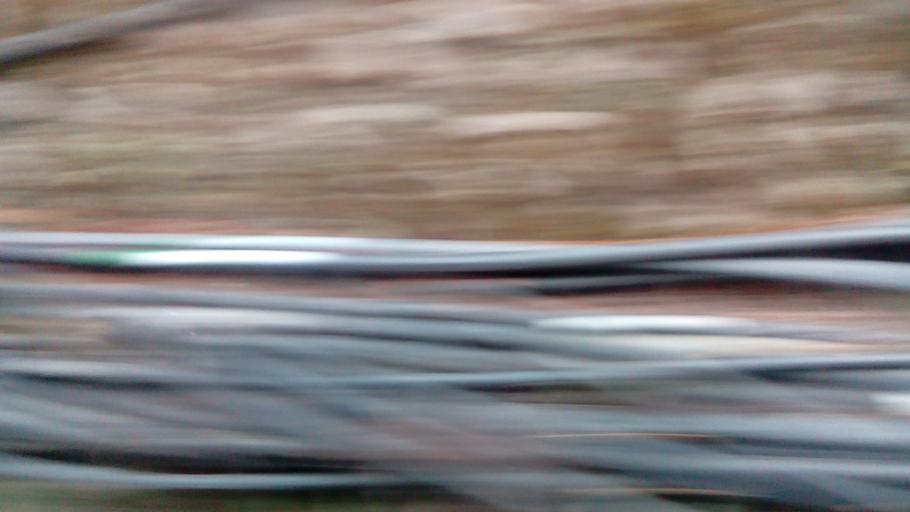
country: TW
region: Taiwan
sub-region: Nantou
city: Puli
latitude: 24.2574
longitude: 121.2543
